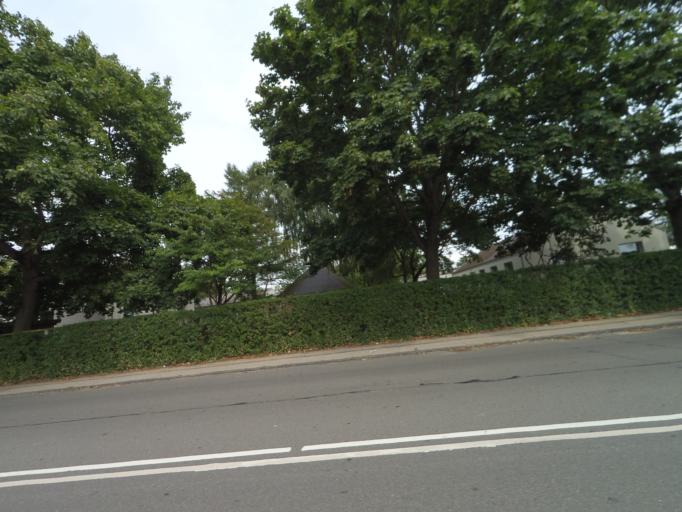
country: DK
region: South Denmark
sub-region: Odense Kommune
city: Bellinge
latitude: 55.3681
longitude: 10.3449
